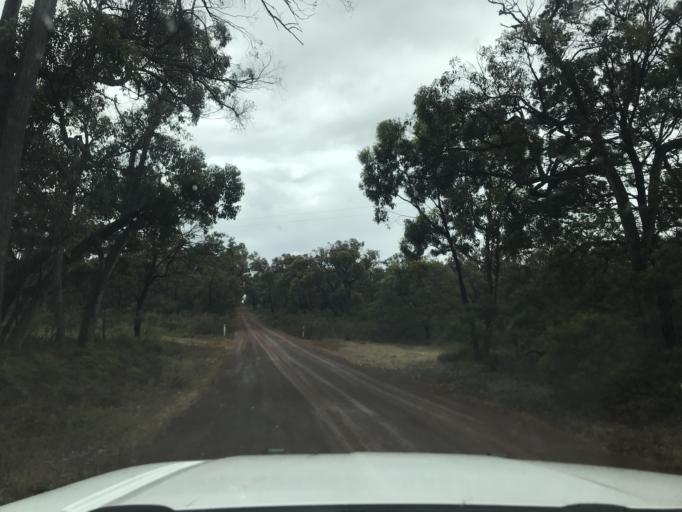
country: AU
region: South Australia
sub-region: Wattle Range
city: Penola
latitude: -37.2401
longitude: 141.3881
